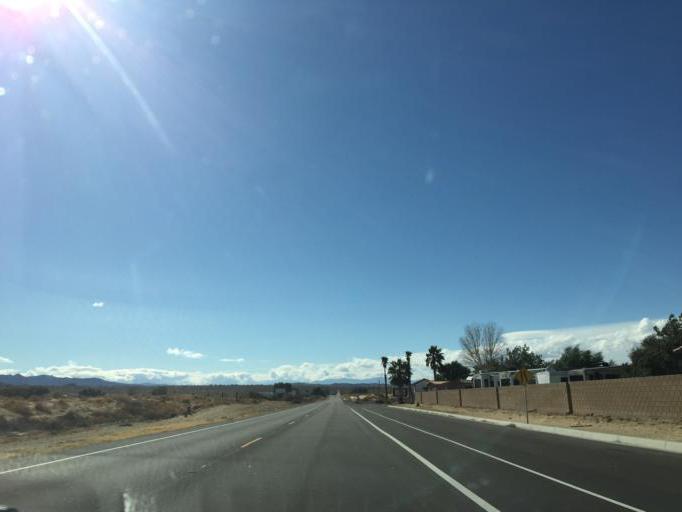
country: US
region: California
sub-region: San Bernardino County
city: Twentynine Palms
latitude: 34.1649
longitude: -116.0437
